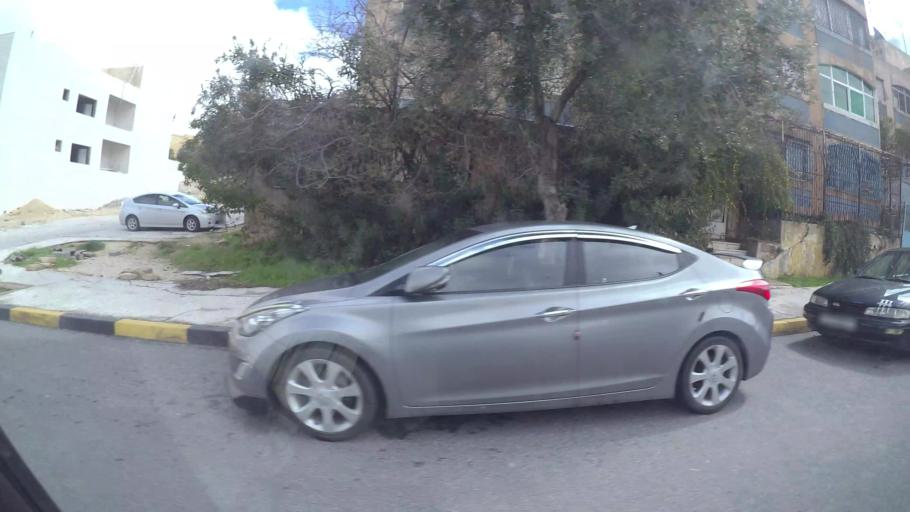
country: JO
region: Amman
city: Al Jubayhah
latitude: 32.0591
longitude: 35.8844
